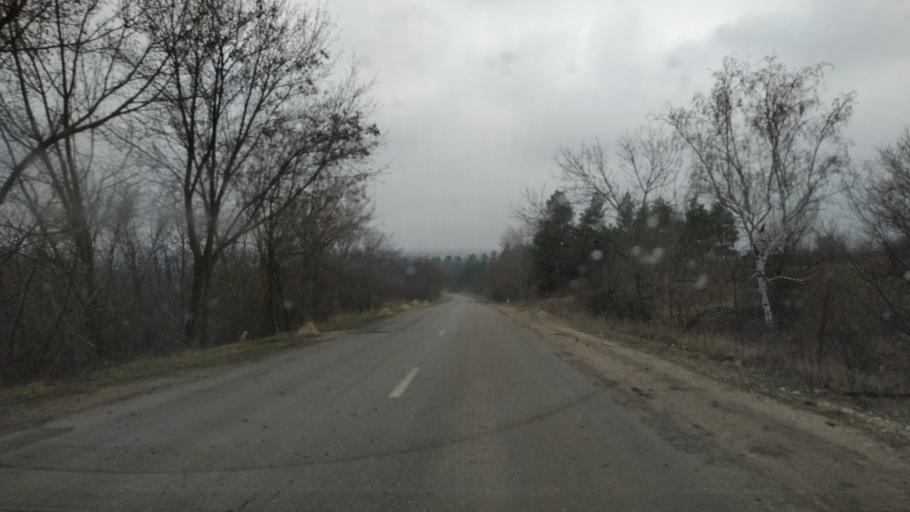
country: MD
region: Cantemir
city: Iargara
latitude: 46.3704
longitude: 28.3743
